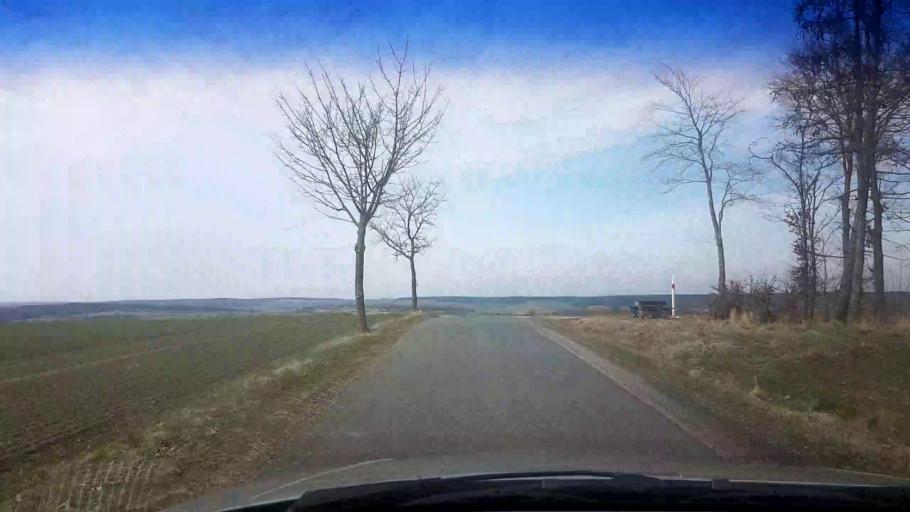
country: DE
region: Bavaria
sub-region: Upper Franconia
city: Burgebrach
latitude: 49.8080
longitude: 10.7604
